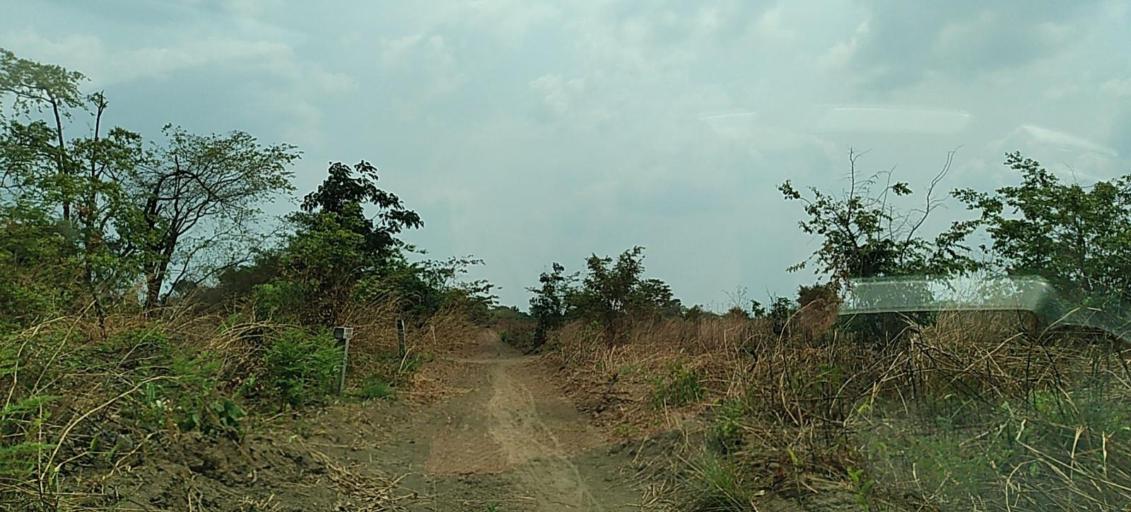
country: ZM
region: Copperbelt
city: Chililabombwe
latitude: -12.3618
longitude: 27.7997
